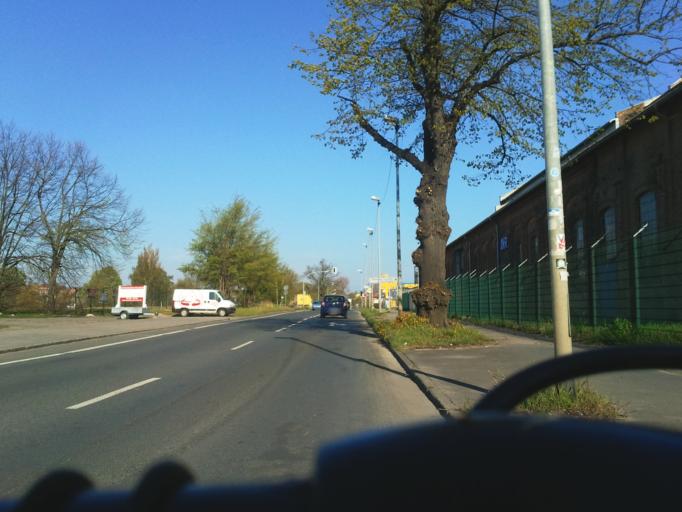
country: DE
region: Mecklenburg-Vorpommern
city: Rostock
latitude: 54.0941
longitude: 12.1055
